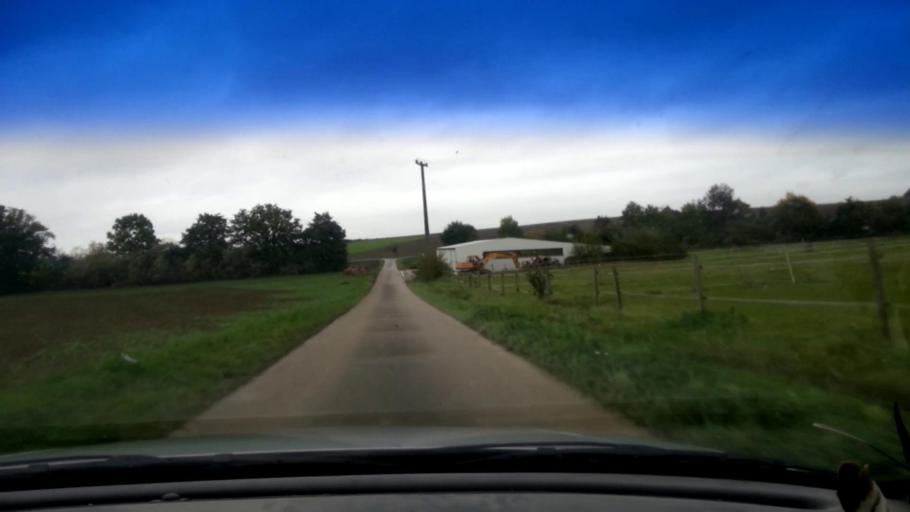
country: DE
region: Bavaria
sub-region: Upper Franconia
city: Litzendorf
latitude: 49.9377
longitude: 11.0045
